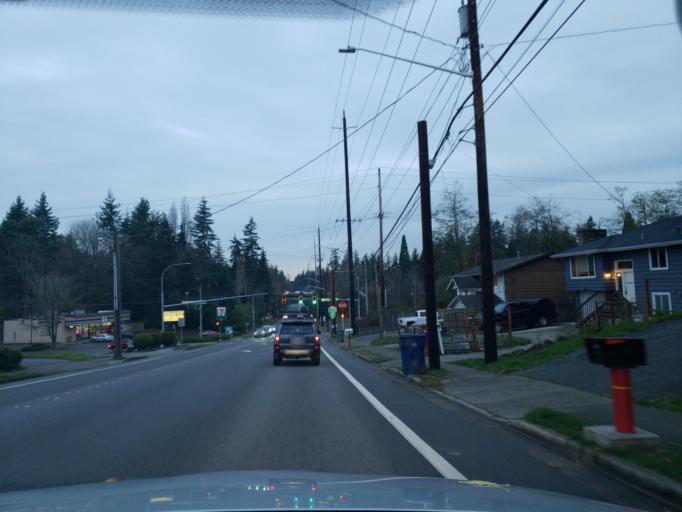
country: US
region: Washington
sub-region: Snohomish County
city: Lynnwood
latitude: 47.8066
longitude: -122.3021
